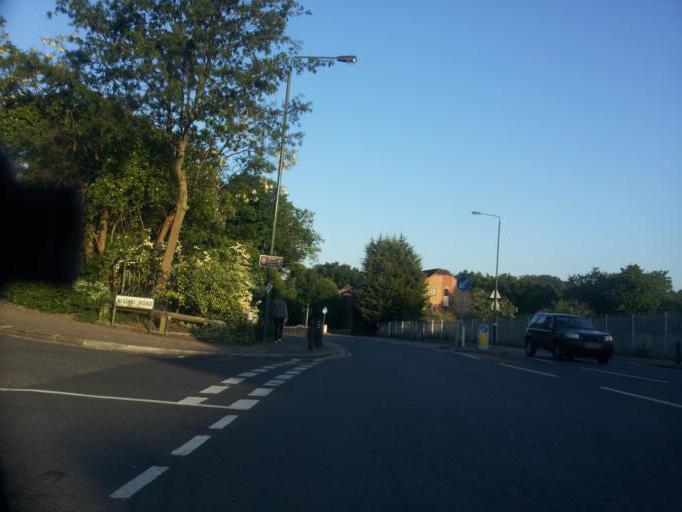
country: GB
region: England
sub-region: Greater London
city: Erith
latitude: 51.4841
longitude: 0.1650
